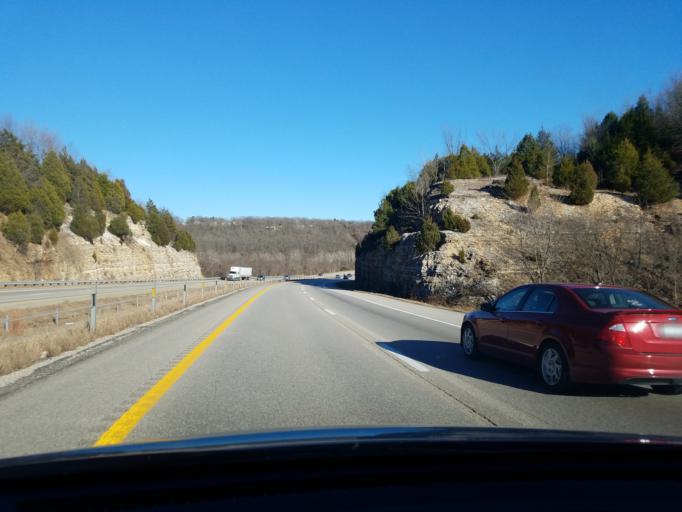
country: US
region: Missouri
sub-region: Pulaski County
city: Waynesville
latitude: 37.8170
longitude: -92.2020
